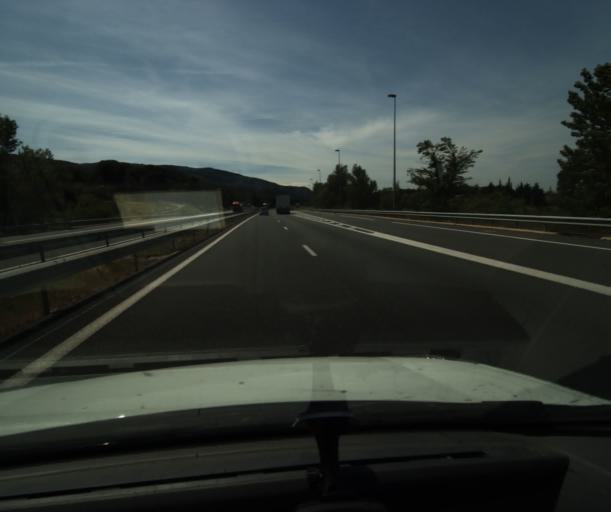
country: FR
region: Languedoc-Roussillon
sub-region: Departement de l'Aude
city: Capendu
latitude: 43.1784
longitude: 2.5478
